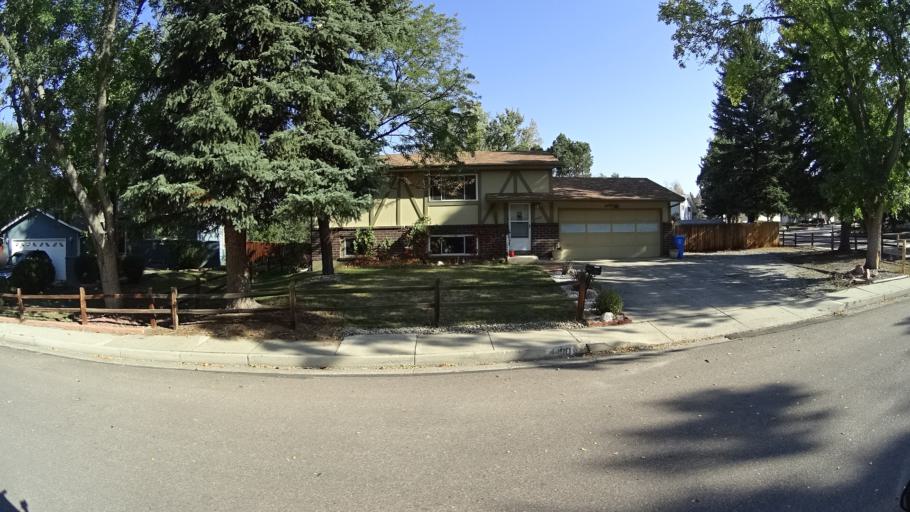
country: US
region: Colorado
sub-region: El Paso County
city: Cimarron Hills
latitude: 38.8782
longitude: -104.7437
